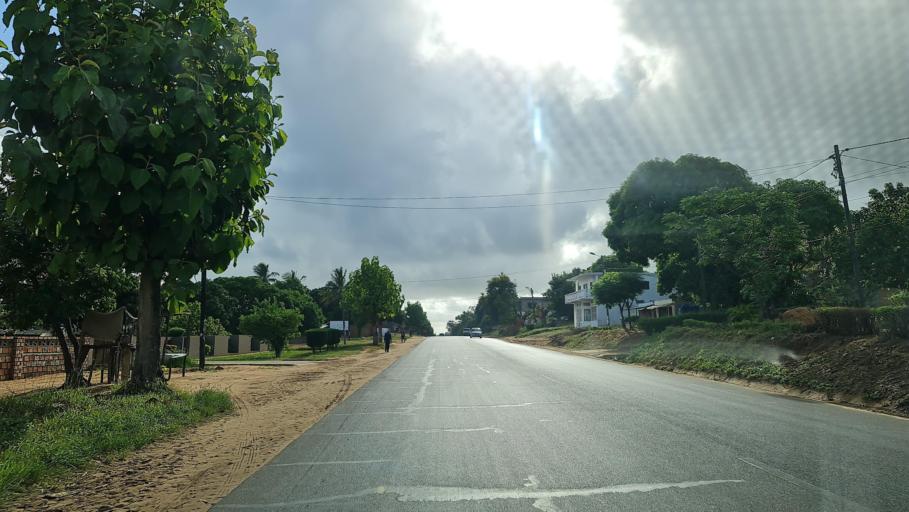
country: MZ
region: Gaza
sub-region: Xai-Xai District
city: Xai-Xai
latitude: -25.0560
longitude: 33.6882
